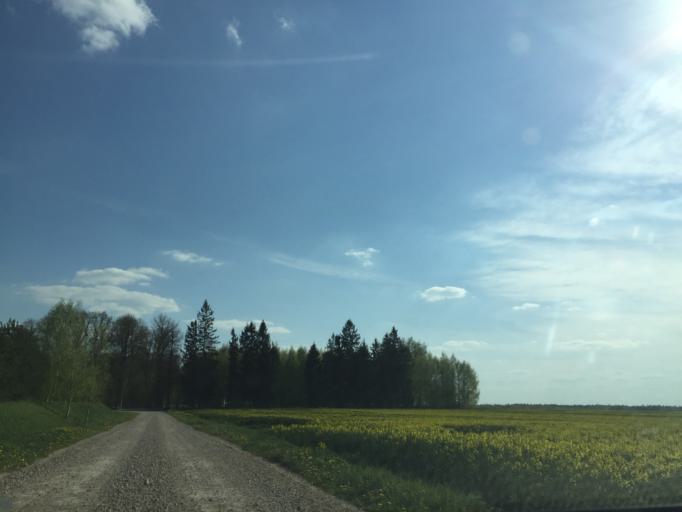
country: LV
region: Bauskas Rajons
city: Bauska
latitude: 56.4921
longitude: 24.3158
